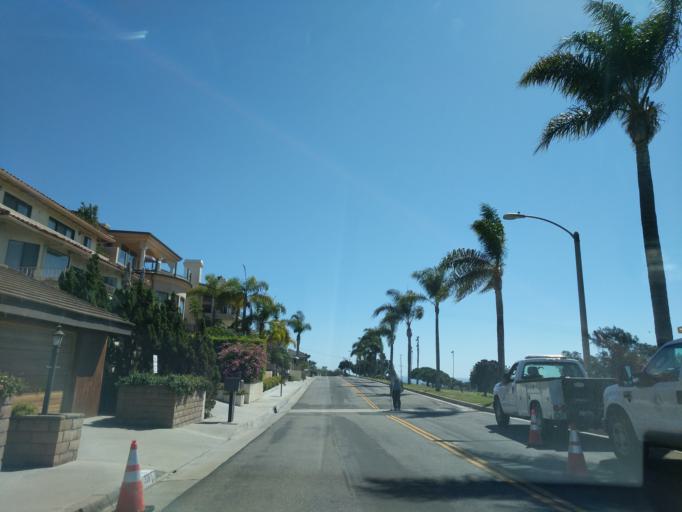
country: US
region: California
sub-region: Orange County
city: San Clemente
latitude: 33.4073
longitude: -117.5926
